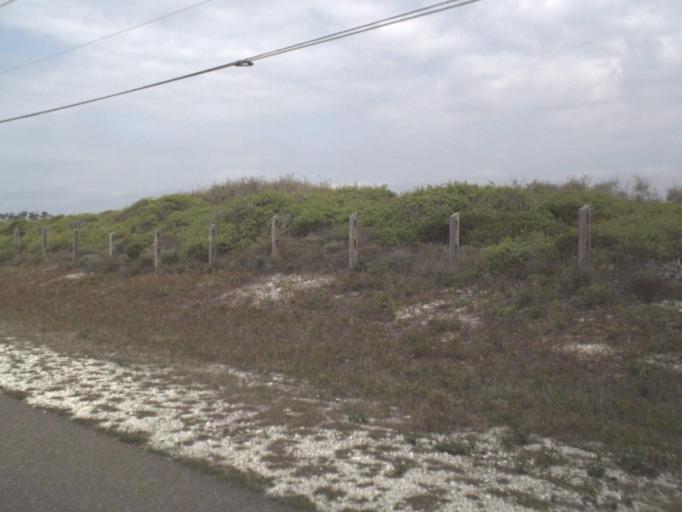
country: US
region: Alabama
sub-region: Baldwin County
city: Orange Beach
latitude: 30.2933
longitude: -87.4575
